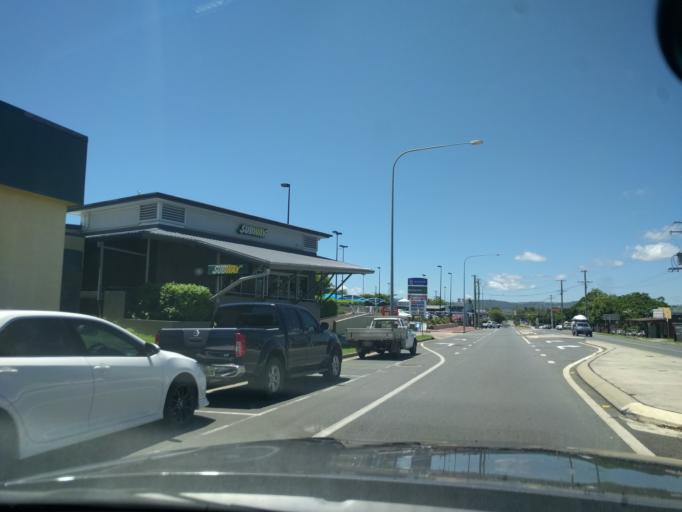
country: AU
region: Queensland
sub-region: Logan
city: Cedar Vale
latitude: -27.9846
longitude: 152.9955
